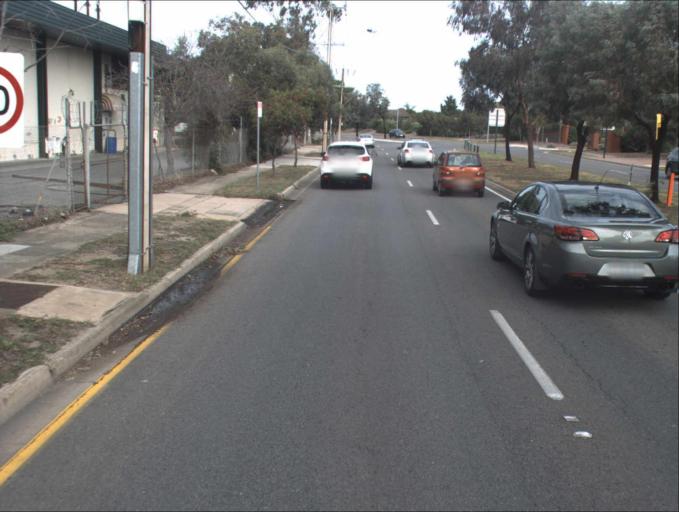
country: AU
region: South Australia
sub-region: Charles Sturt
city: West Lakes Shore
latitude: -34.8601
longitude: 138.5028
